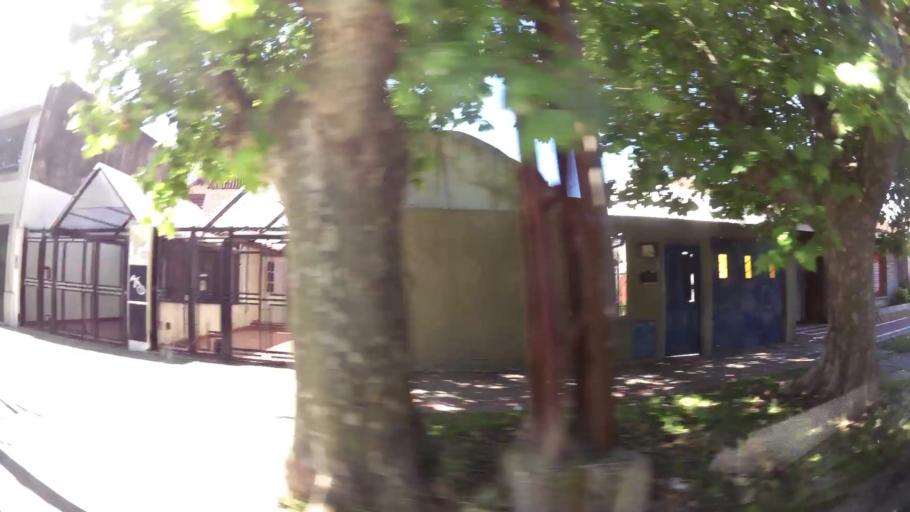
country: AR
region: Buenos Aires
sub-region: Partido de Lomas de Zamora
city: Lomas de Zamora
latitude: -34.7521
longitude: -58.4093
